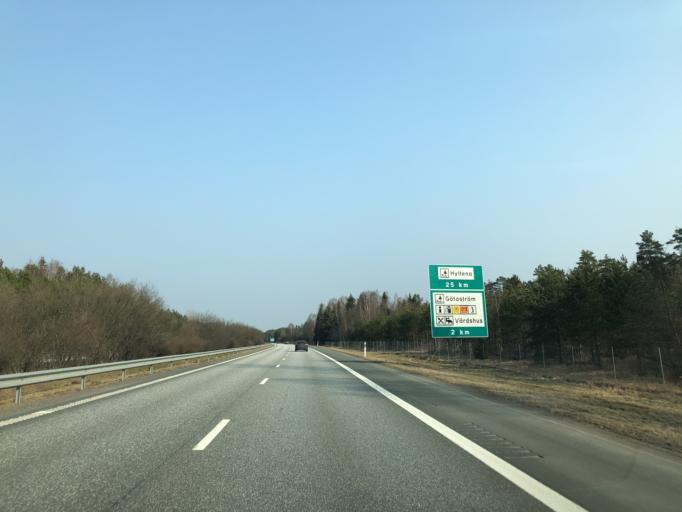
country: SE
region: Joenkoeping
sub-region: Vaggeryds Kommun
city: Skillingaryd
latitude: 57.4291
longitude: 14.1042
